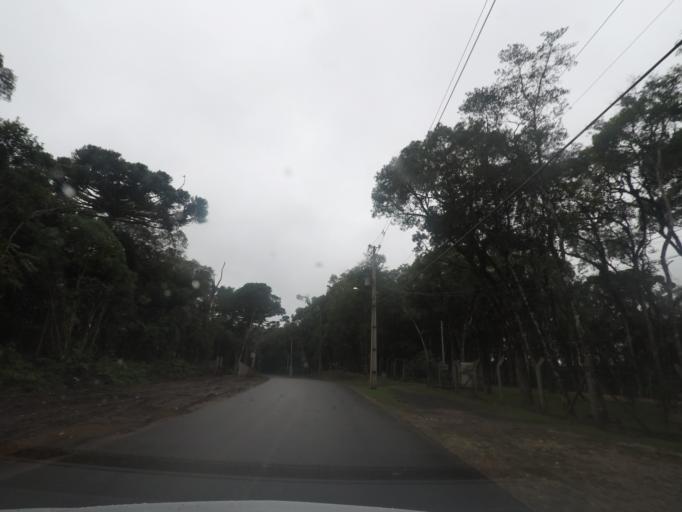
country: BR
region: Parana
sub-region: Campina Grande Do Sul
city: Campina Grande do Sul
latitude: -25.3062
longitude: -49.1365
